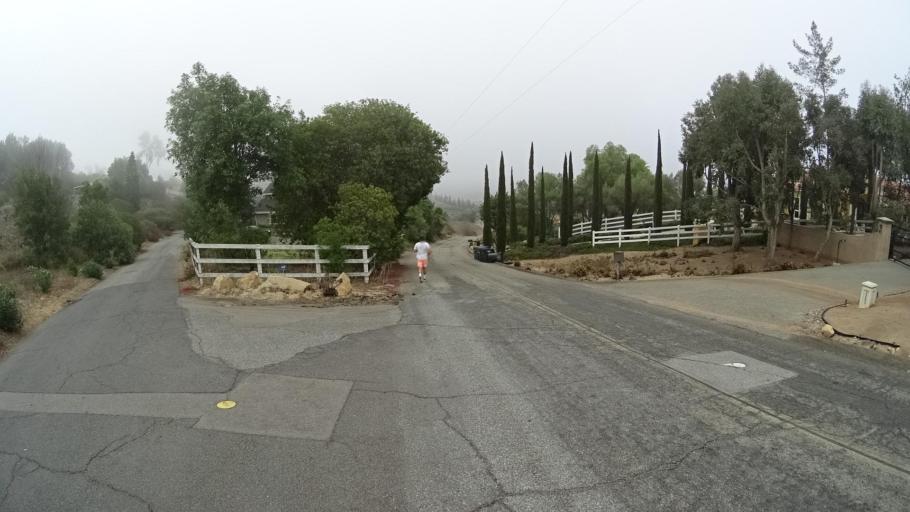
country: US
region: California
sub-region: San Diego County
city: Bonsall
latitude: 33.3297
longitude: -117.1740
